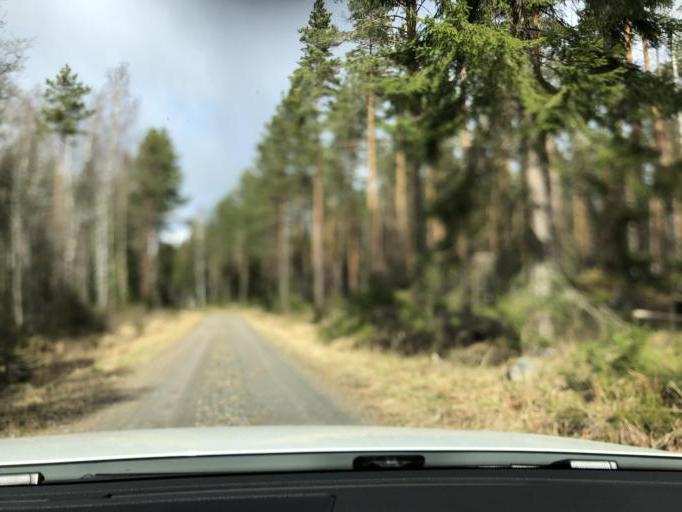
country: SE
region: Gaevleborg
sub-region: Gavle Kommun
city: Hedesunda
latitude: 60.3316
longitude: 17.1077
